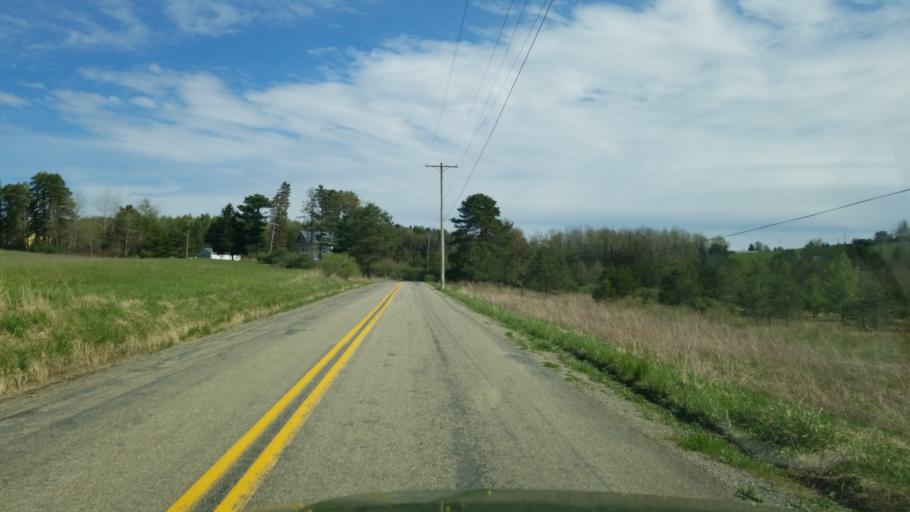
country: US
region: Pennsylvania
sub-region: Jefferson County
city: Brockway
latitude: 41.2222
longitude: -78.8489
